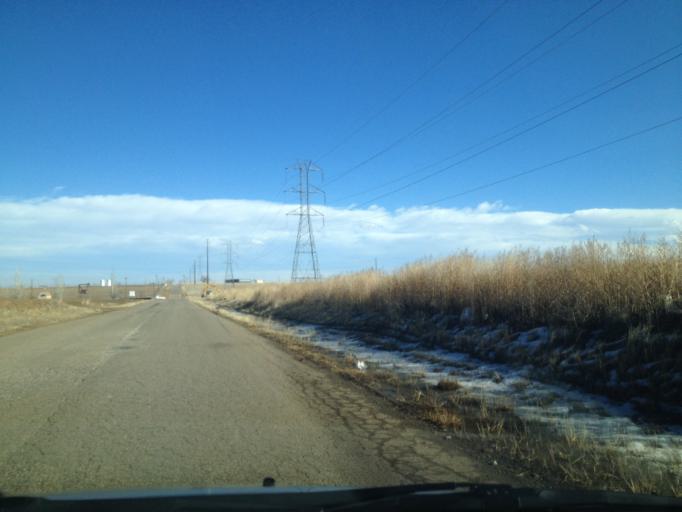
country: US
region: Colorado
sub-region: Weld County
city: Dacono
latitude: 40.0584
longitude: -104.9783
